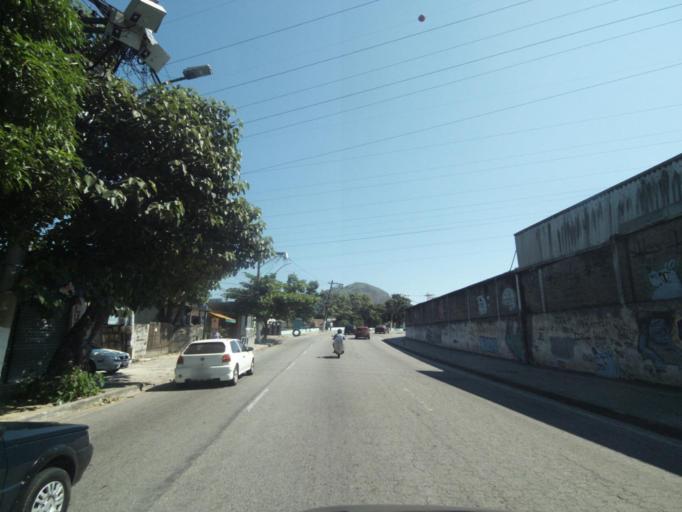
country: BR
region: Rio de Janeiro
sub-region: Niteroi
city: Niteroi
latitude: -22.9059
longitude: -43.0655
